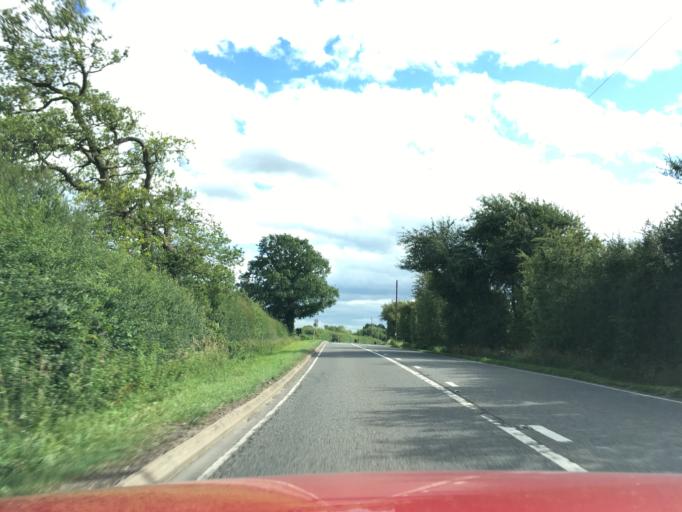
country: GB
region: England
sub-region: Warwickshire
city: Hartshill
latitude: 52.5639
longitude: -1.4823
